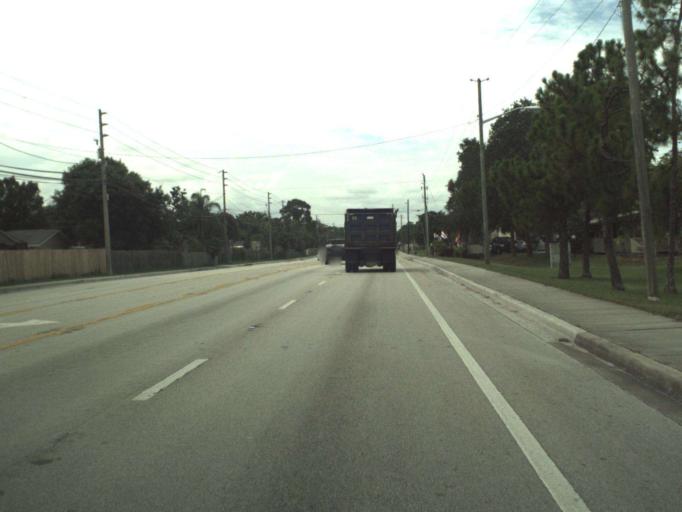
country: US
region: Florida
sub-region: Saint Lucie County
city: Fort Pierce South
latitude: 27.4236
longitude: -80.3504
